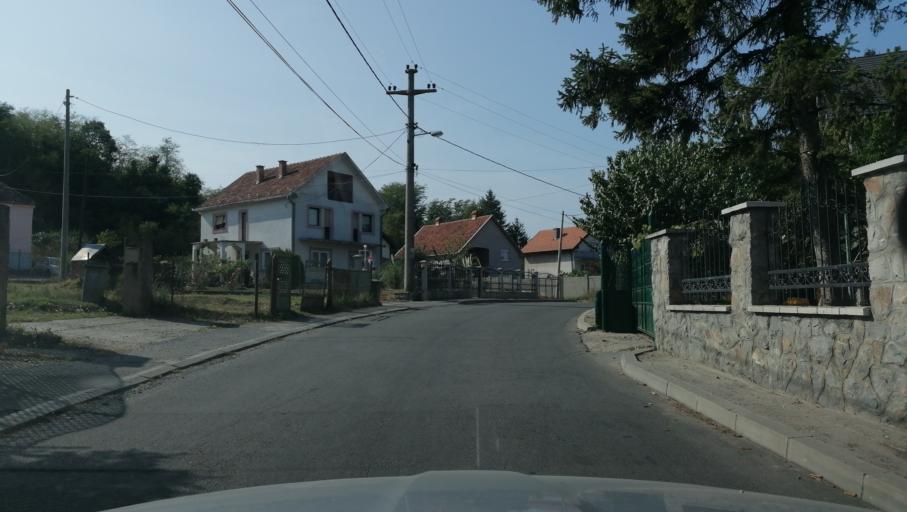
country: RS
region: Central Serbia
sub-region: Belgrade
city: Grocka
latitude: 44.6615
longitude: 20.5915
